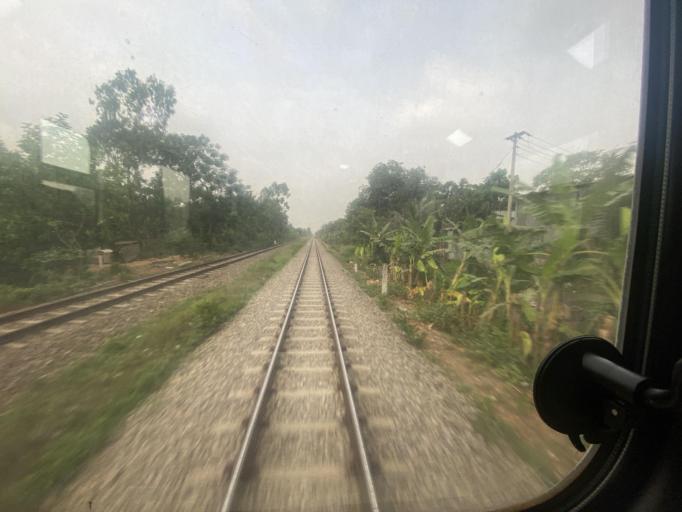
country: BD
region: Dhaka
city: Tungi
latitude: 23.9322
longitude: 90.4636
